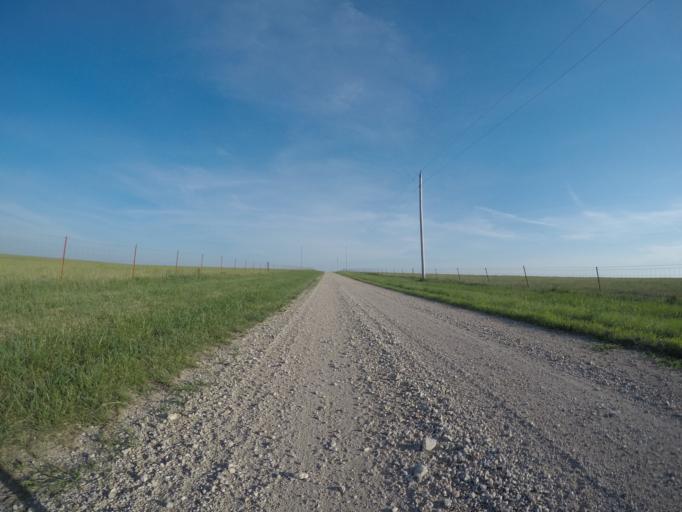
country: US
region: Kansas
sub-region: Riley County
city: Manhattan
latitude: 39.0127
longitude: -96.4919
